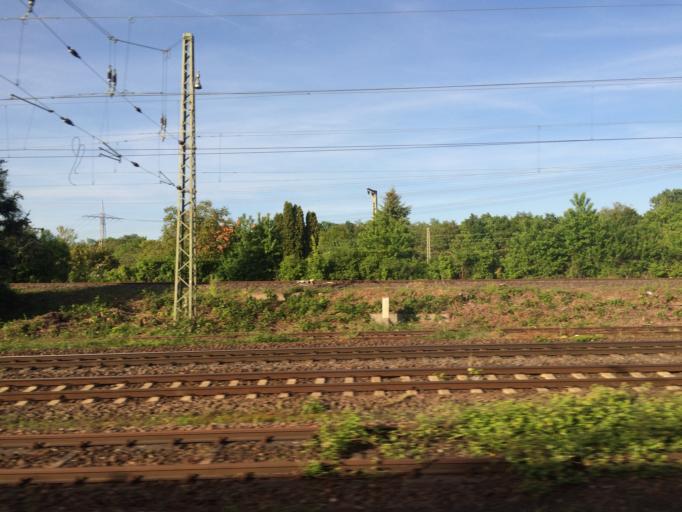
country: DE
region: Hesse
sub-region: Regierungsbezirk Darmstadt
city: Wiesbaden
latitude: 50.0423
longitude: 8.2546
